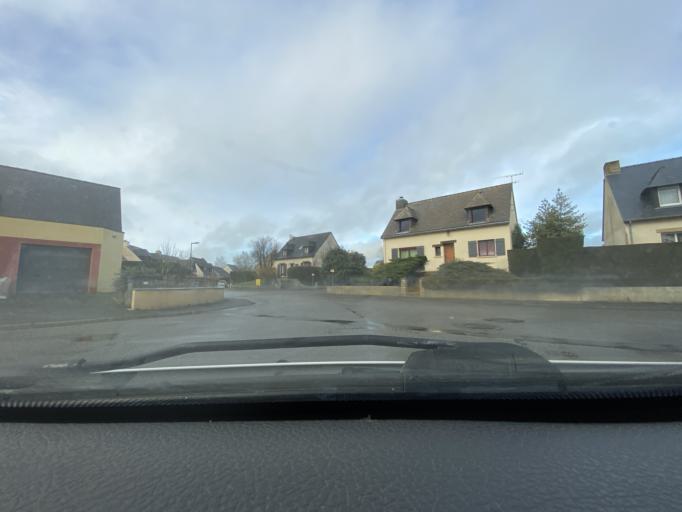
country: FR
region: Brittany
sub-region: Departement d'Ille-et-Vilaine
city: Melesse
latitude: 48.2226
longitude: -1.7033
